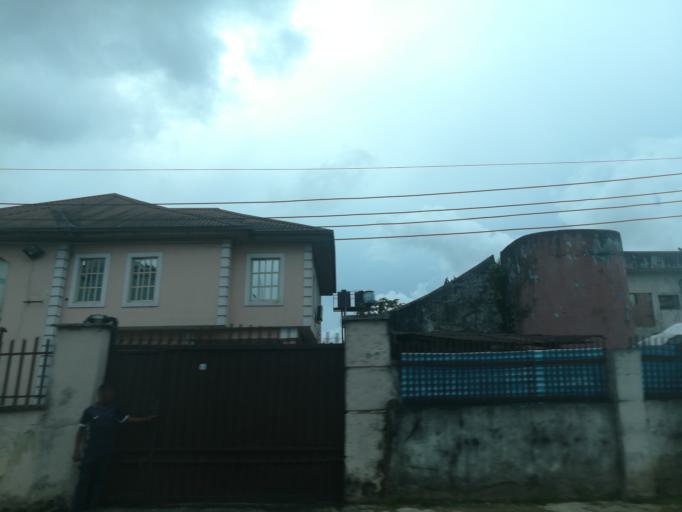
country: NG
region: Rivers
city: Port Harcourt
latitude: 4.8197
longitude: 6.9995
